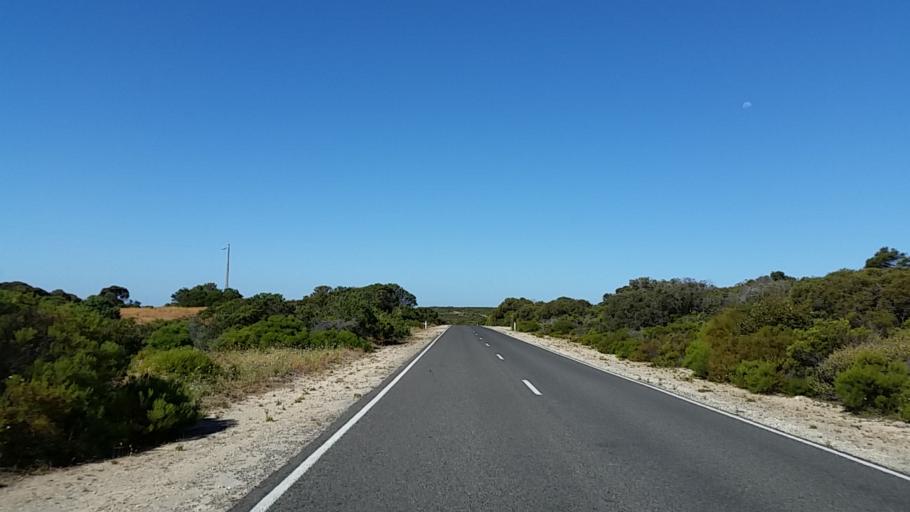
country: AU
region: South Australia
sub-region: Yorke Peninsula
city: Honiton
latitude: -35.2603
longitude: 136.9582
